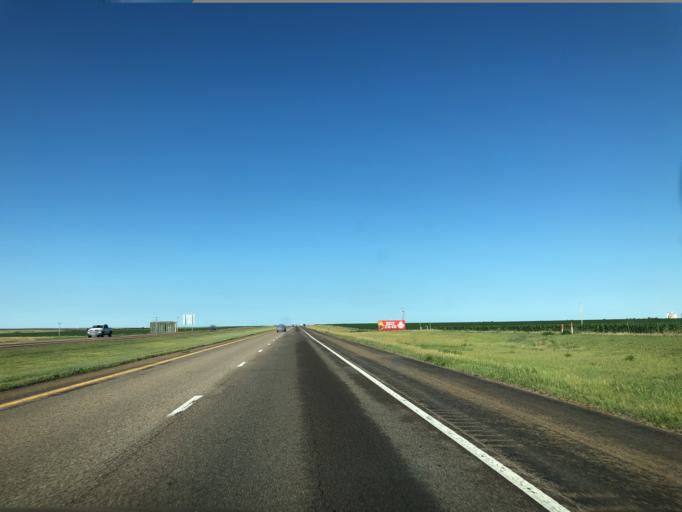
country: US
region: Kansas
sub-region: Thomas County
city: Colby
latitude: 39.3589
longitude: -101.3320
